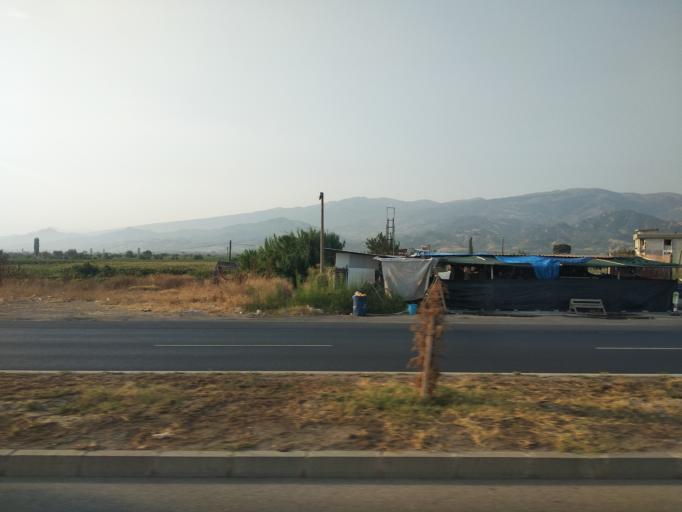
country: TR
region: Manisa
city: Salihli
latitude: 38.4960
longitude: 28.1853
